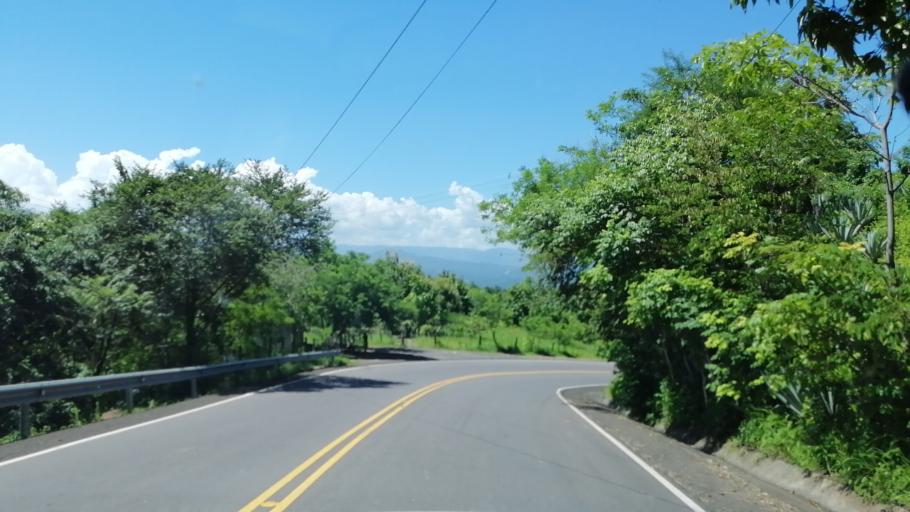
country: SV
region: San Miguel
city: Ciudad Barrios
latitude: 13.8091
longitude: -88.1906
